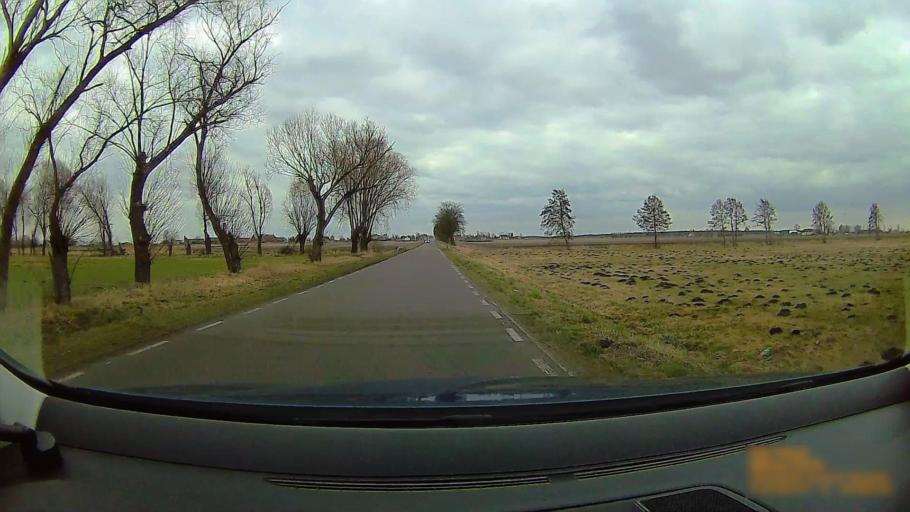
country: PL
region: Greater Poland Voivodeship
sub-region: Powiat koninski
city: Rychwal
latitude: 52.1001
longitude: 18.1012
